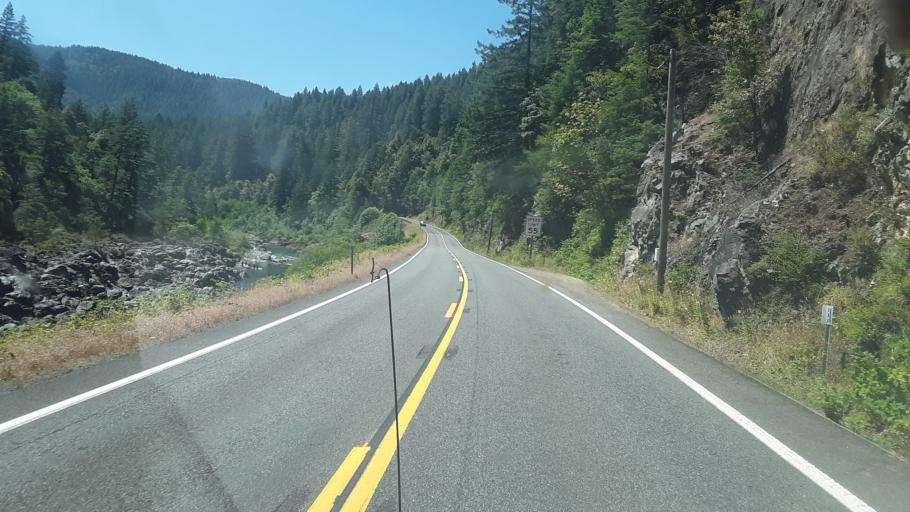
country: US
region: California
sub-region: Del Norte County
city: Bertsch-Oceanview
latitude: 41.8378
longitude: -124.0363
